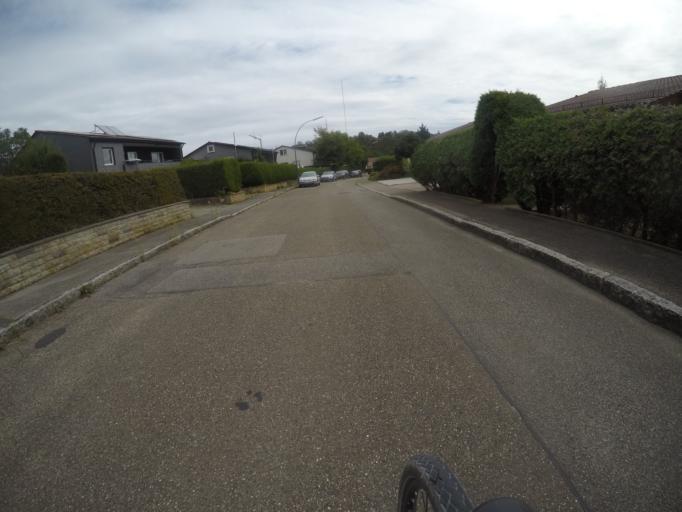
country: DE
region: Baden-Wuerttemberg
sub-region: Karlsruhe Region
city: Muhlacker
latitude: 48.9414
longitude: 8.8362
